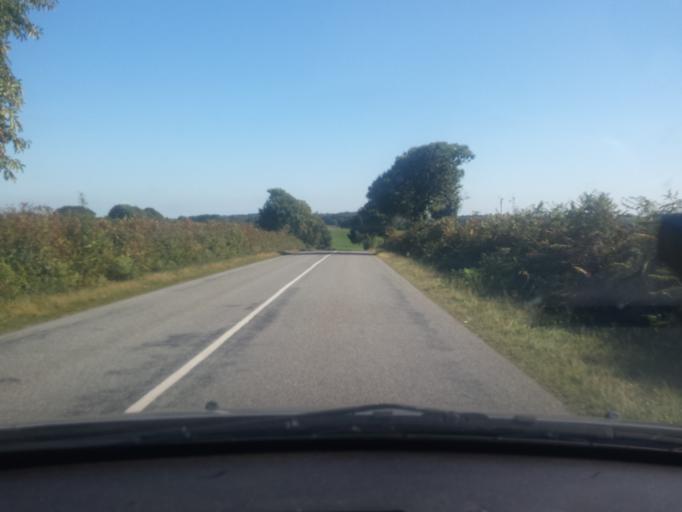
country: FR
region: Brittany
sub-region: Departement du Morbihan
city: Cleguerec
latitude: 48.1206
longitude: -3.1337
